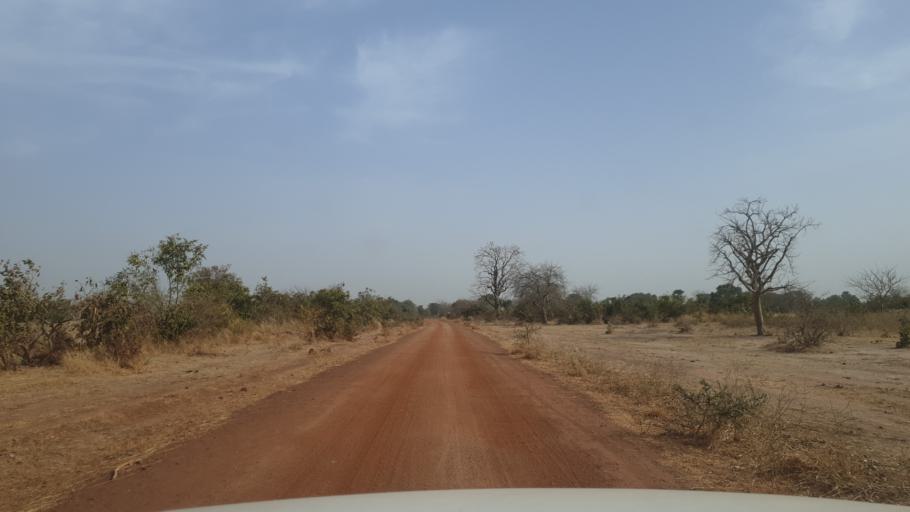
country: ML
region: Koulikoro
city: Kolokani
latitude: 13.3131
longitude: -8.2785
